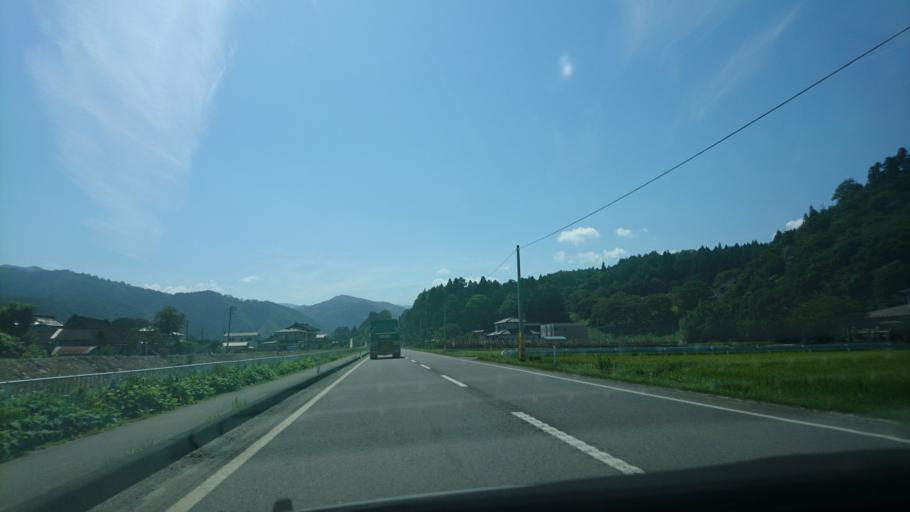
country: JP
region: Iwate
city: Ofunato
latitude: 39.0279
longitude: 141.5916
